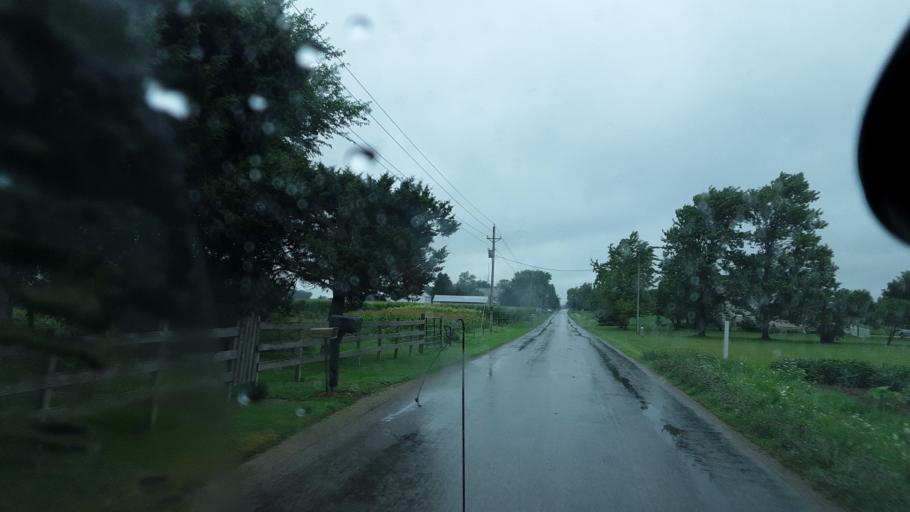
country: US
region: Indiana
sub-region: Adams County
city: Berne
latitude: 40.7123
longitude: -84.8532
